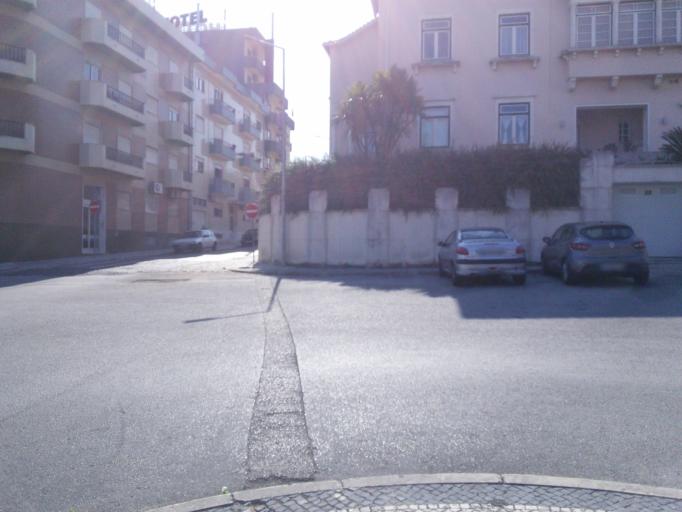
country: PT
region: Leiria
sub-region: Leiria
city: Leiria
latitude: 39.7417
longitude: -8.8051
